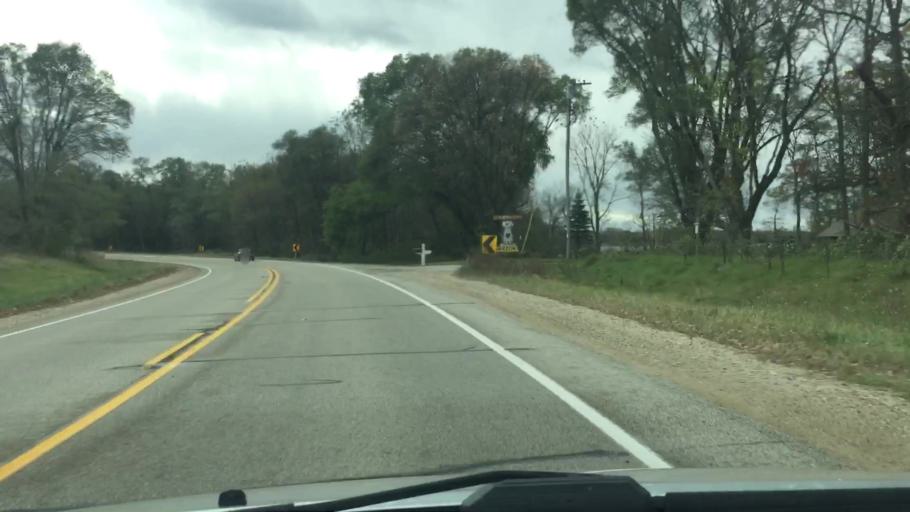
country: US
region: Wisconsin
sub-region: Waukesha County
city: Eagle
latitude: 42.9452
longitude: -88.4785
